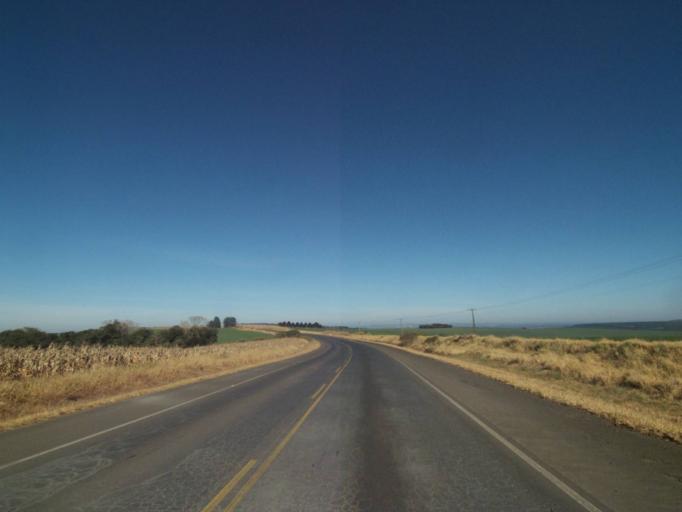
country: BR
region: Parana
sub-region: Tibagi
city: Tibagi
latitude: -24.3811
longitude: -50.3305
